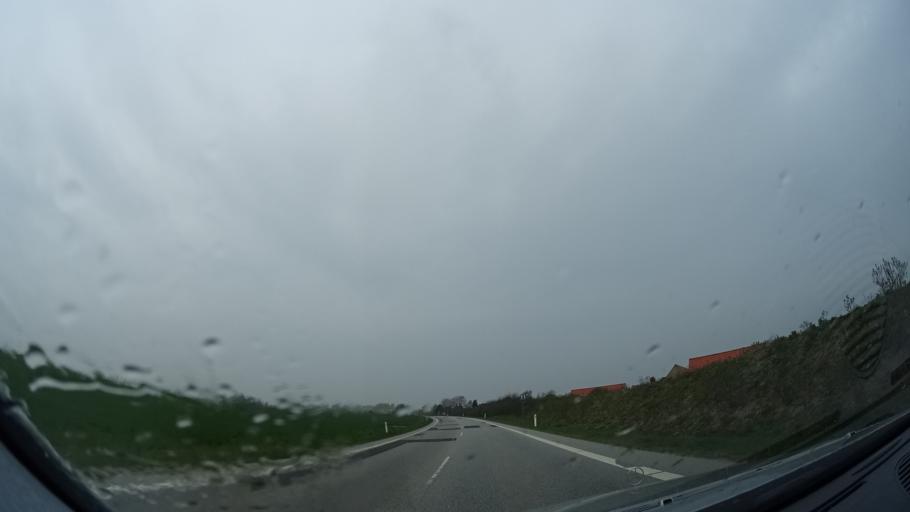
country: DK
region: Zealand
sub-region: Holbaek Kommune
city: Vipperod
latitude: 55.7026
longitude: 11.7761
